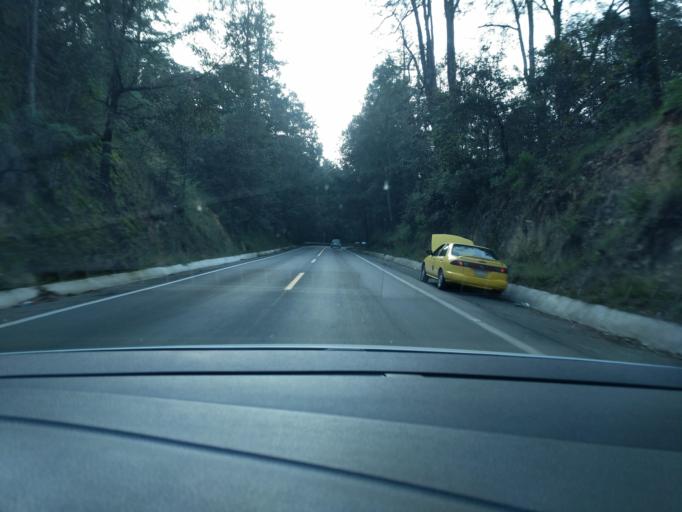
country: MX
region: Hidalgo
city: Mineral del Monte
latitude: 20.1465
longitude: -98.6766
